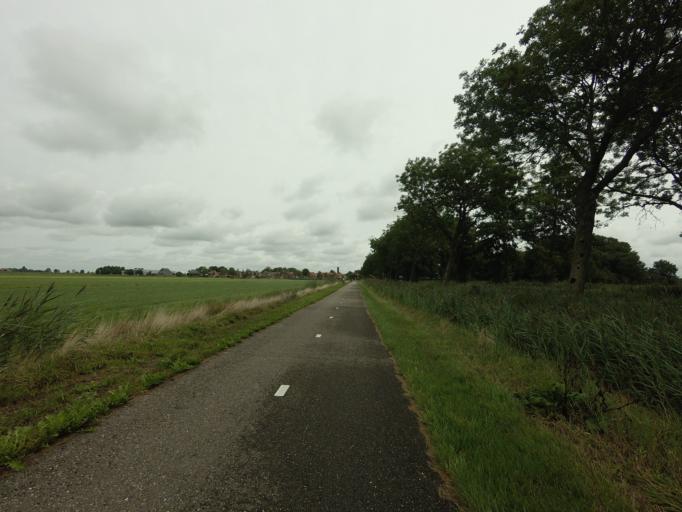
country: NL
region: Overijssel
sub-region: Gemeente Steenwijkerland
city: Oldemarkt
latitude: 52.8058
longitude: 5.9119
